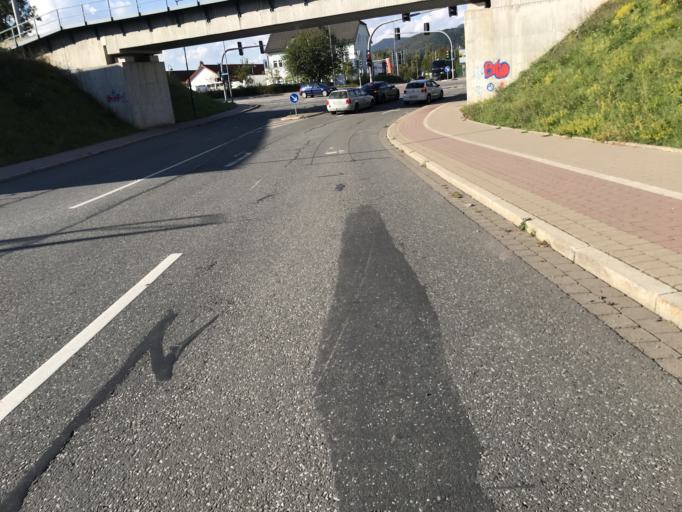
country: DE
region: Hesse
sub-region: Regierungsbezirk Kassel
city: Eschwege
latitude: 51.1919
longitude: 10.0391
